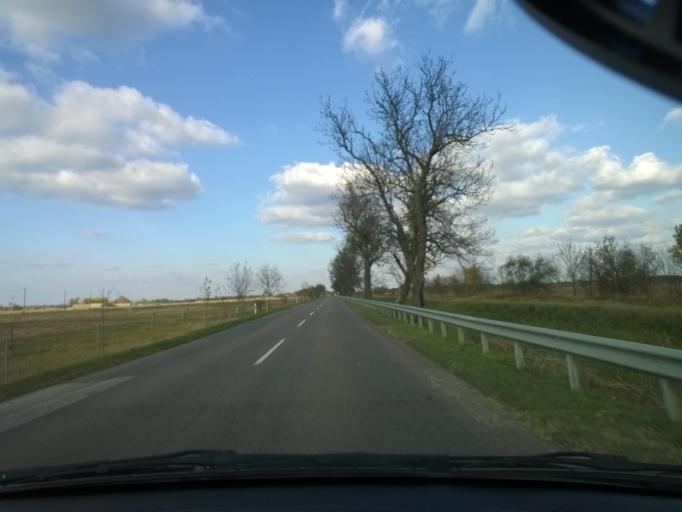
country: HU
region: Csongrad
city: Szegvar
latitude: 46.5304
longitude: 20.3130
